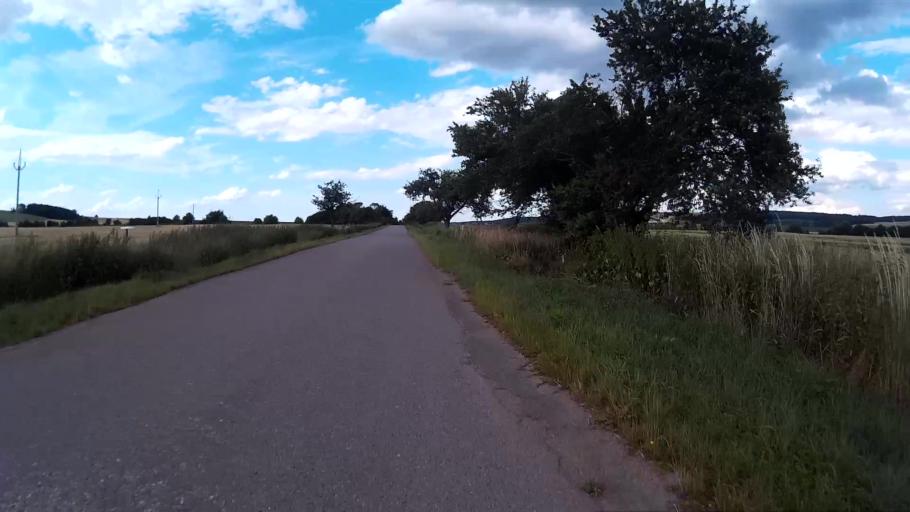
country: CZ
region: South Moravian
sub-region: Okres Brno-Venkov
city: Rosice
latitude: 49.1952
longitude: 16.3971
